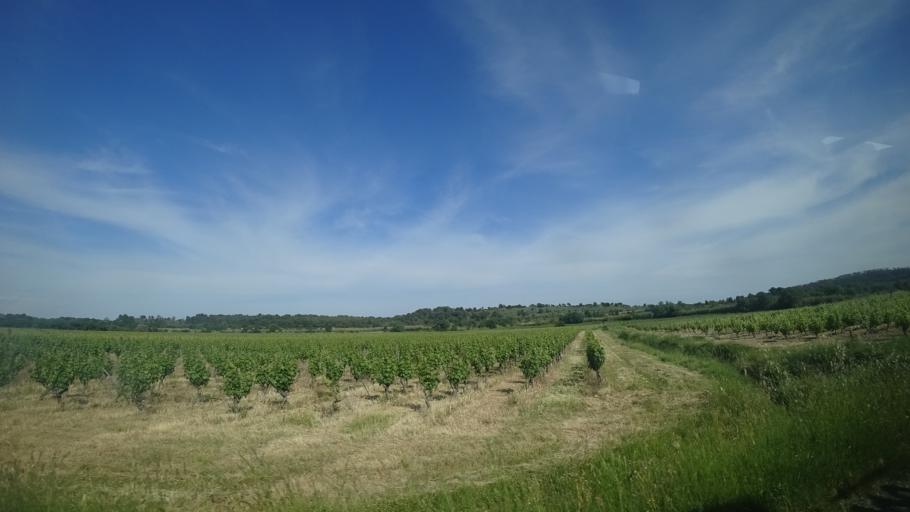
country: FR
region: Languedoc-Roussillon
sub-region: Departement de l'Aude
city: Ginestas
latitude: 43.2792
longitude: 2.8168
